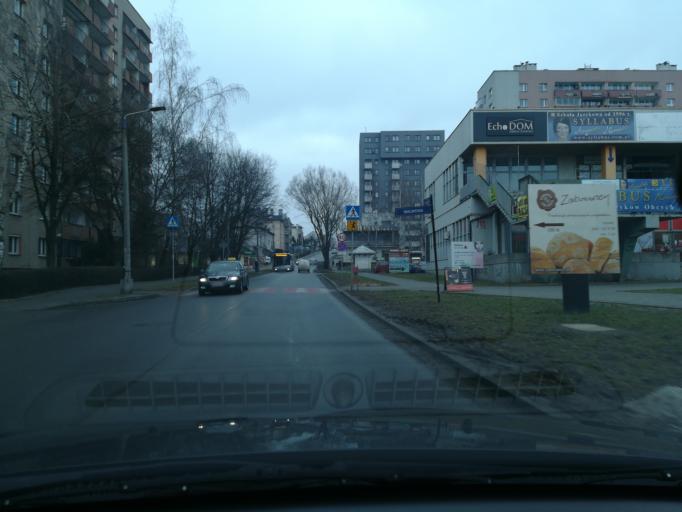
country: PL
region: Lesser Poland Voivodeship
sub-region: Krakow
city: Krakow
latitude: 50.0156
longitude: 19.9504
